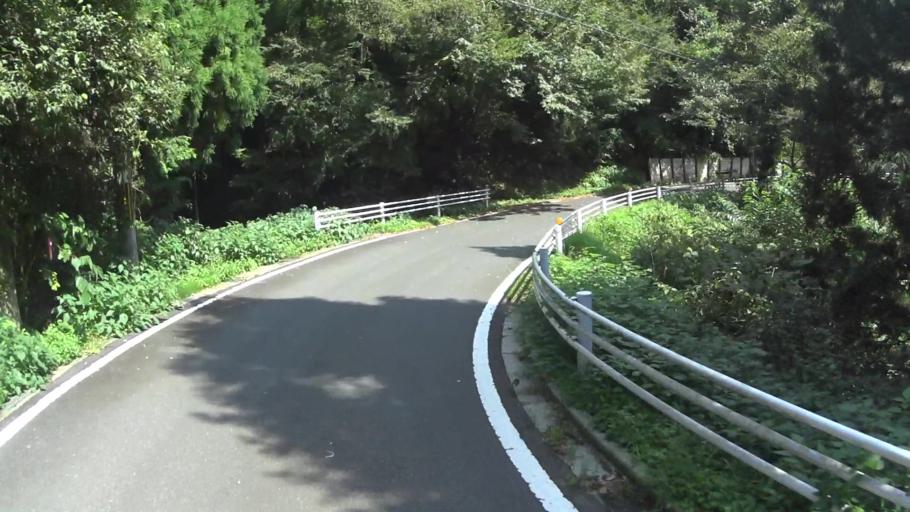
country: JP
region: Kyoto
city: Miyazu
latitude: 35.6825
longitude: 135.2348
